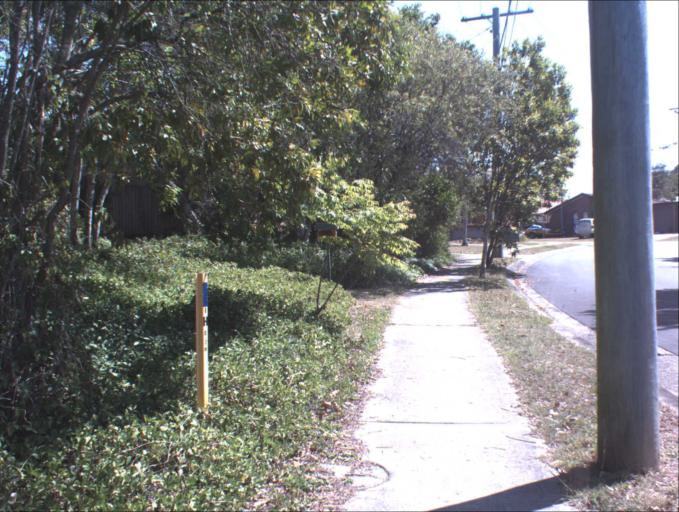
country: AU
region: Queensland
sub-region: Logan
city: Rochedale South
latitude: -27.5899
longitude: 153.1292
